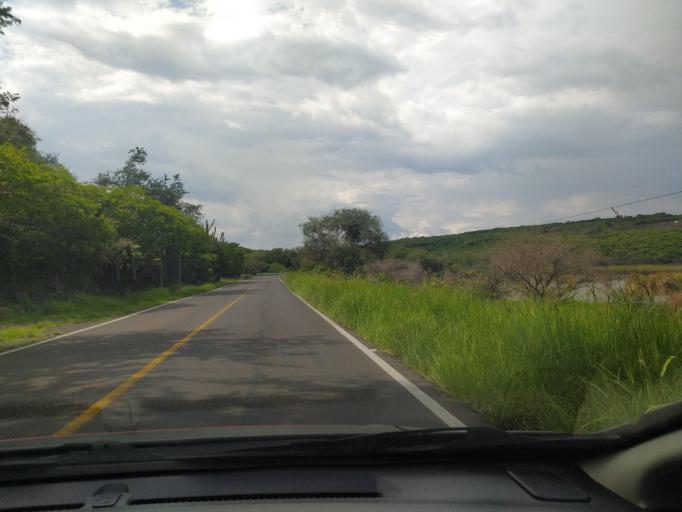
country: MX
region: Jalisco
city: Villa Corona
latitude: 20.3670
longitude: -103.6698
